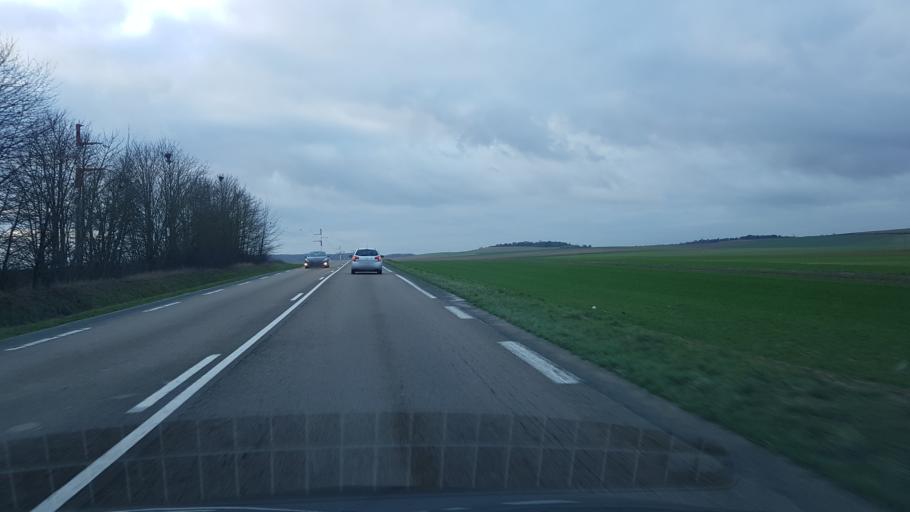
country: FR
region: Champagne-Ardenne
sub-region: Departement de la Marne
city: Sezanne
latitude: 48.7209
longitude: 3.7786
